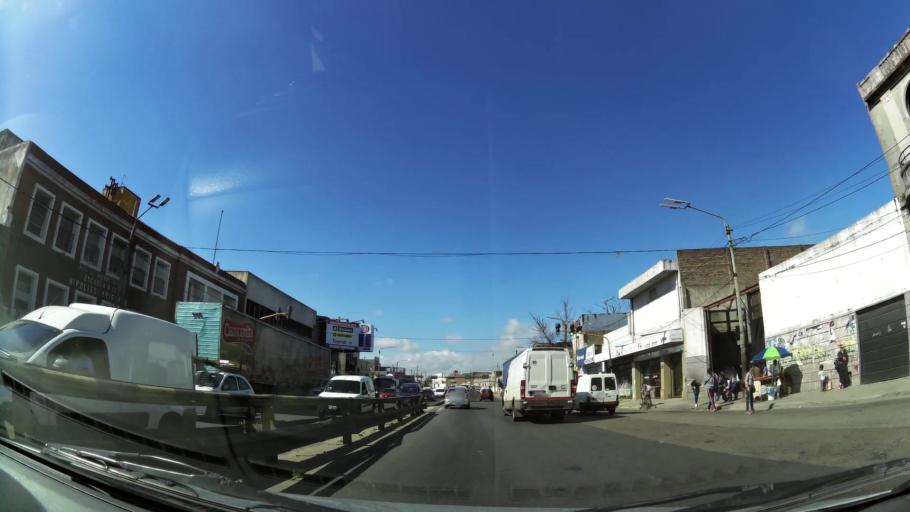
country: AR
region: Buenos Aires
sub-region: Partido de Lanus
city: Lanus
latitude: -34.6632
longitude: -58.4174
